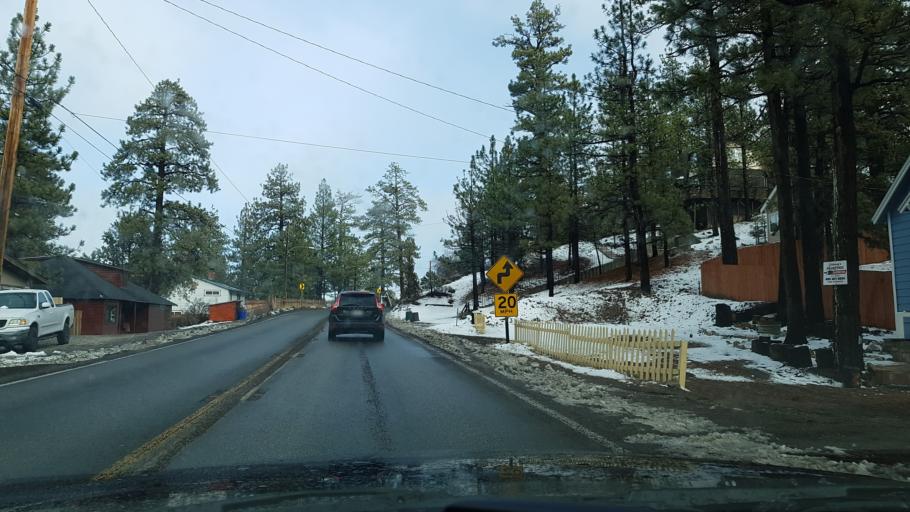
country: US
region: California
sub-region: San Bernardino County
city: Big Bear City
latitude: 34.2604
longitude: -116.8593
